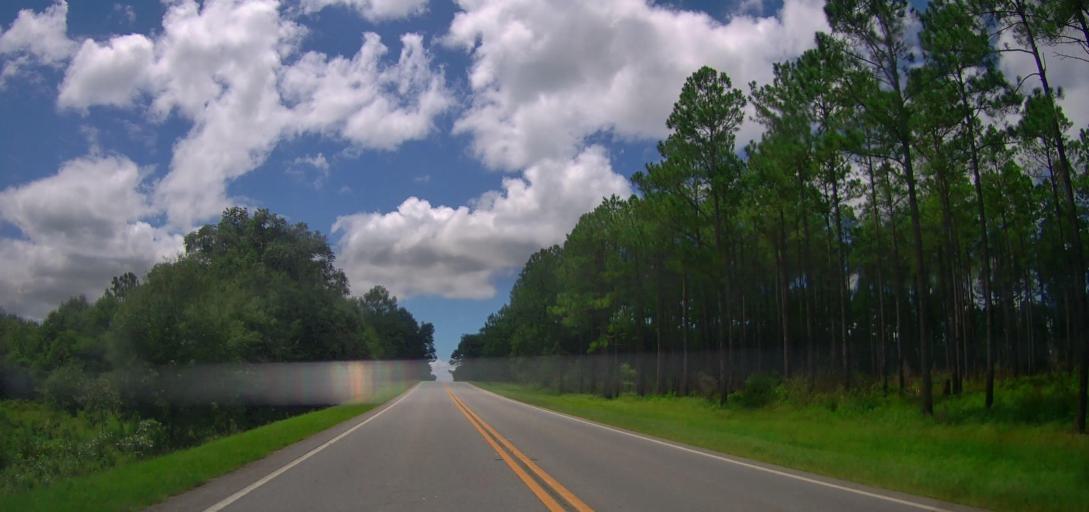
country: US
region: Georgia
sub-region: Turner County
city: Ashburn
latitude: 31.7223
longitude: -83.5632
